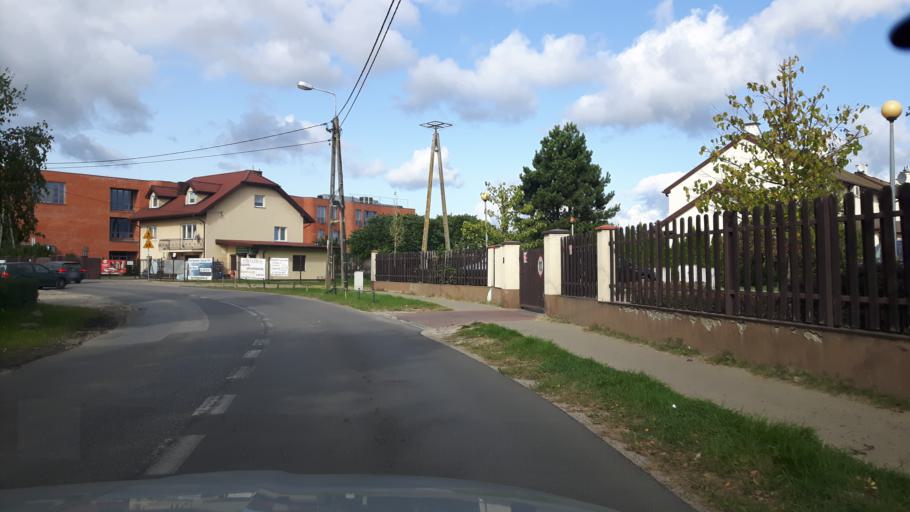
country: PL
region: Masovian Voivodeship
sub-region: Powiat legionowski
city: Stanislawow Pierwszy
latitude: 52.3617
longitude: 21.0488
